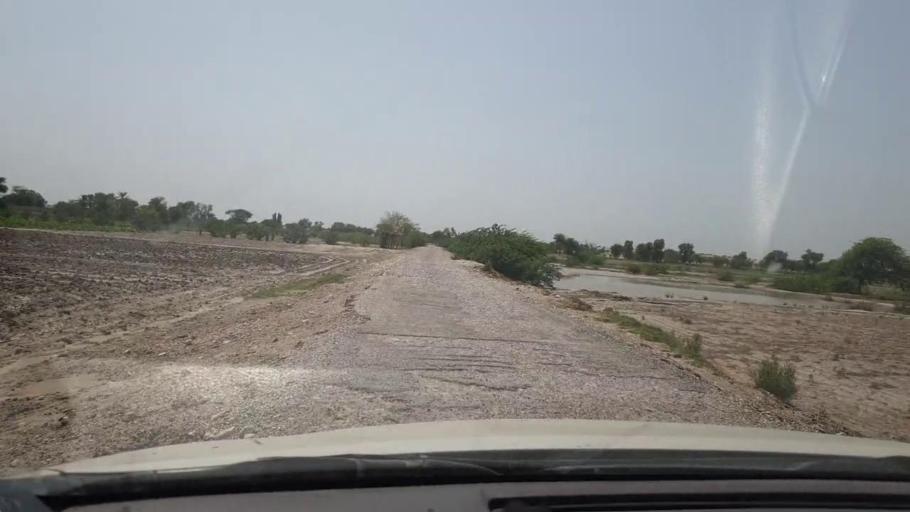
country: PK
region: Sindh
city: Rohri
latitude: 27.5212
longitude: 69.0965
